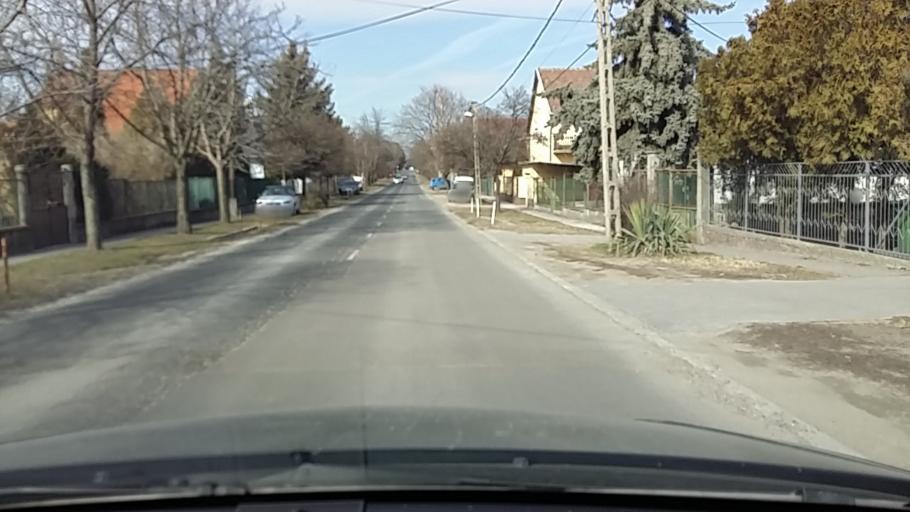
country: HU
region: Budapest
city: Budapest XXIII. keruelet
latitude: 47.3962
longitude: 19.0919
